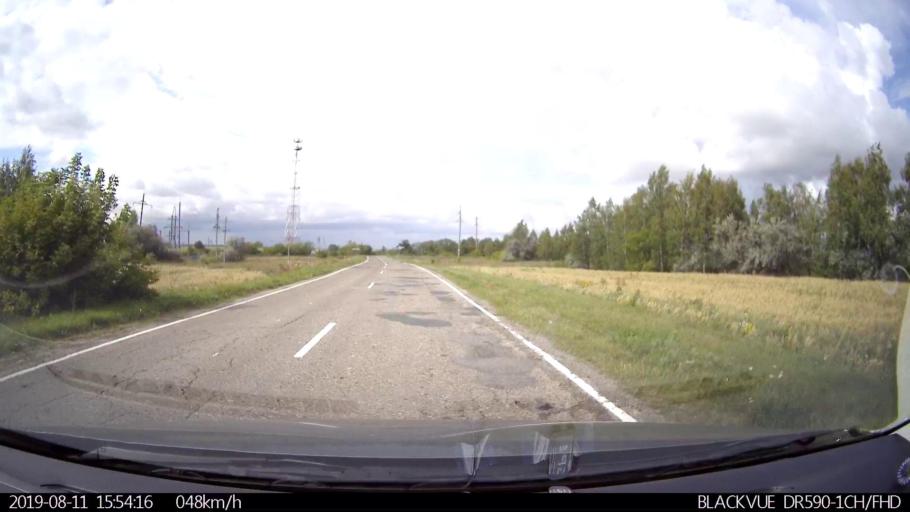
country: RU
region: Ulyanovsk
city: Ignatovka
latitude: 53.9402
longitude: 47.6567
